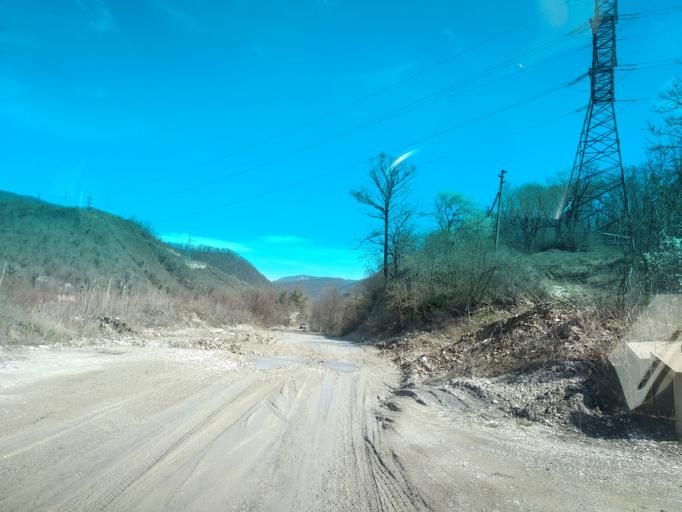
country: RU
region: Krasnodarskiy
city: Shepsi
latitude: 44.0576
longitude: 39.1671
